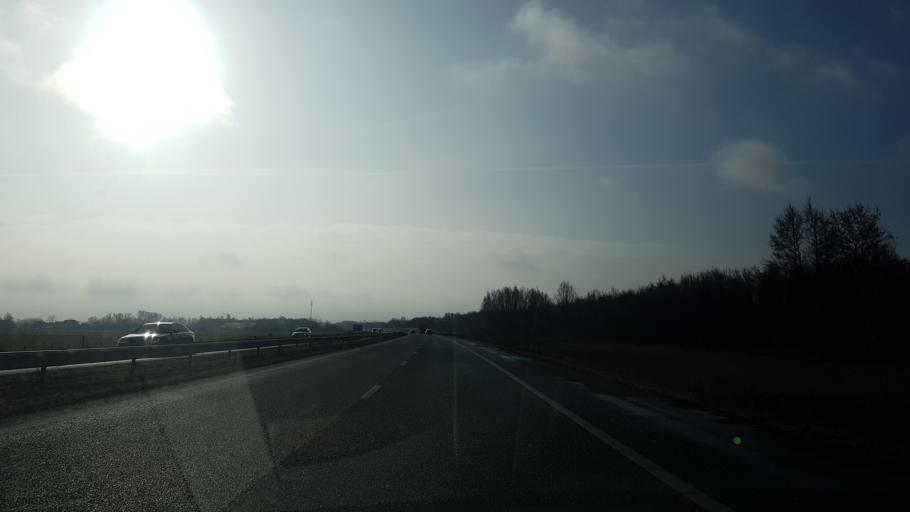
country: NL
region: Friesland
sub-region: Gemeente Skarsterlan
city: Oudehaske
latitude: 53.0001
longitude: 5.8763
